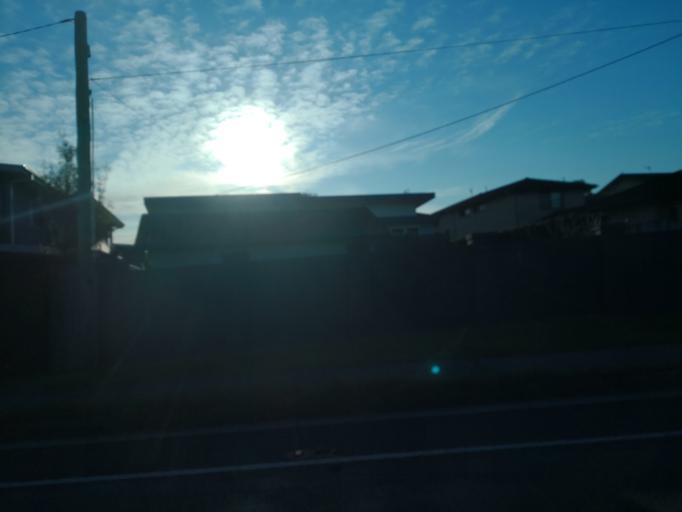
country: AU
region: New South Wales
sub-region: Gosford Shire
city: Narara
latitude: -33.4083
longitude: 151.3506
